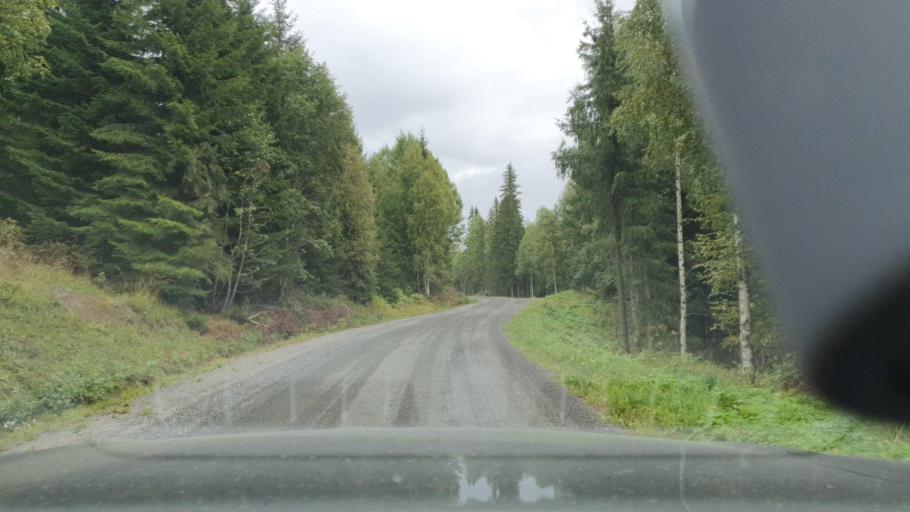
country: SE
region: Vaermland
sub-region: Torsby Kommun
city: Torsby
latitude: 60.3950
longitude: 12.6593
